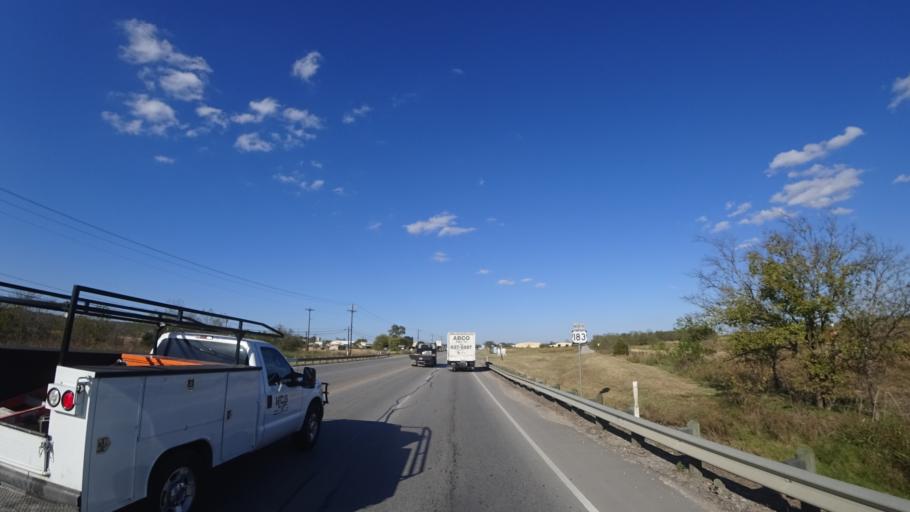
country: US
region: Texas
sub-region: Travis County
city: Onion Creek
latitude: 30.1503
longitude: -97.6968
